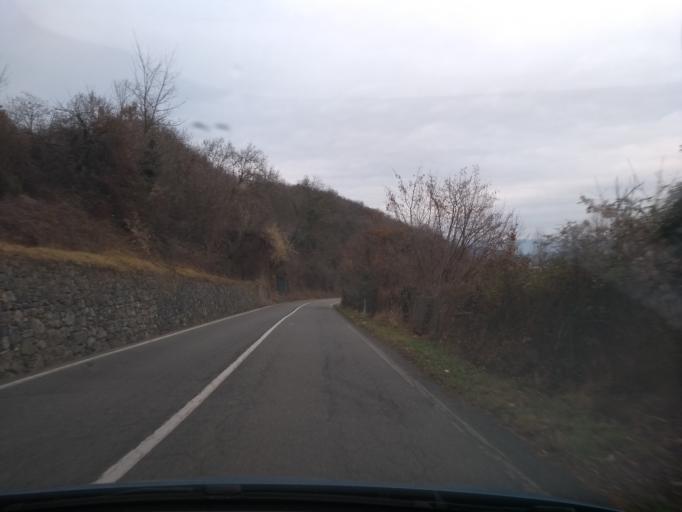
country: IT
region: Piedmont
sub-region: Provincia di Torino
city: Colleretto Giacosa
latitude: 45.4358
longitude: 7.7994
